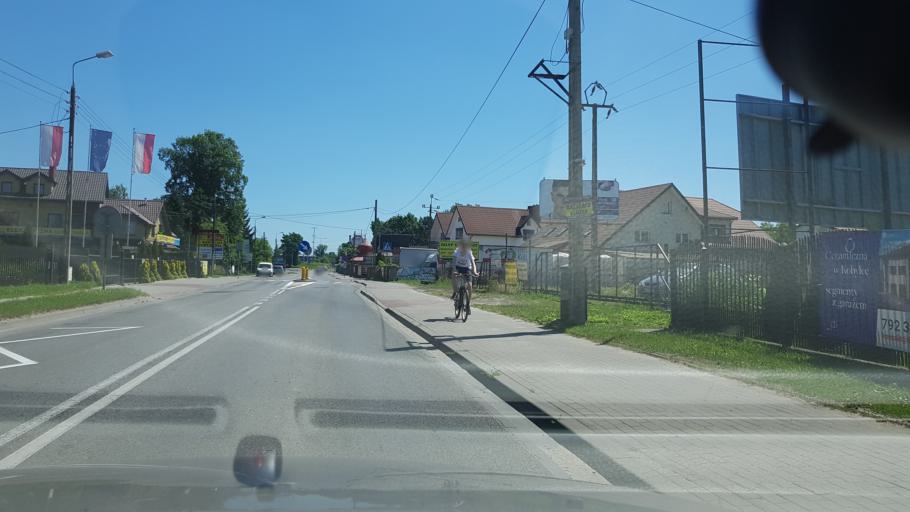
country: PL
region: Masovian Voivodeship
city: Zielonka
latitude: 52.3117
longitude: 21.1357
